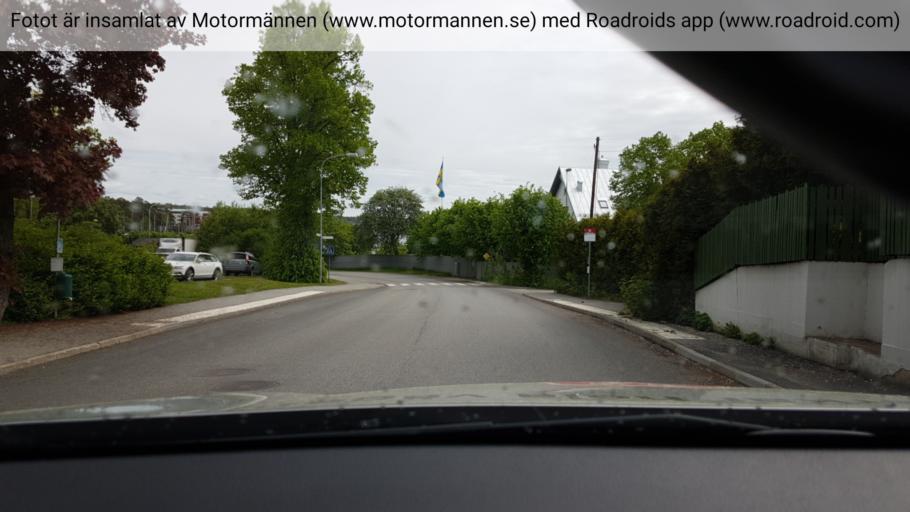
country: SE
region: Stockholm
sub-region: Nacka Kommun
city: Saltsjobaden
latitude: 59.2733
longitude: 18.3073
